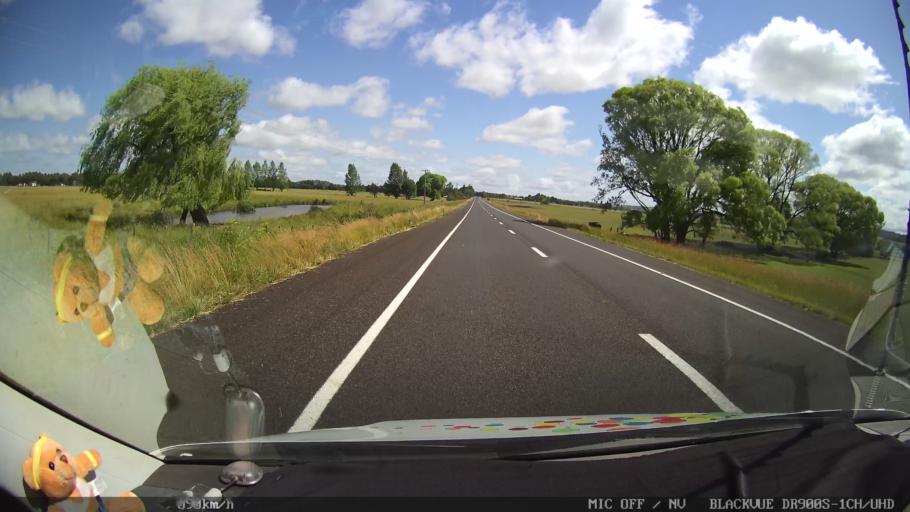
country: AU
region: New South Wales
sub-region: Glen Innes Severn
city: Glen Innes
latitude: -29.8308
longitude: 151.7378
